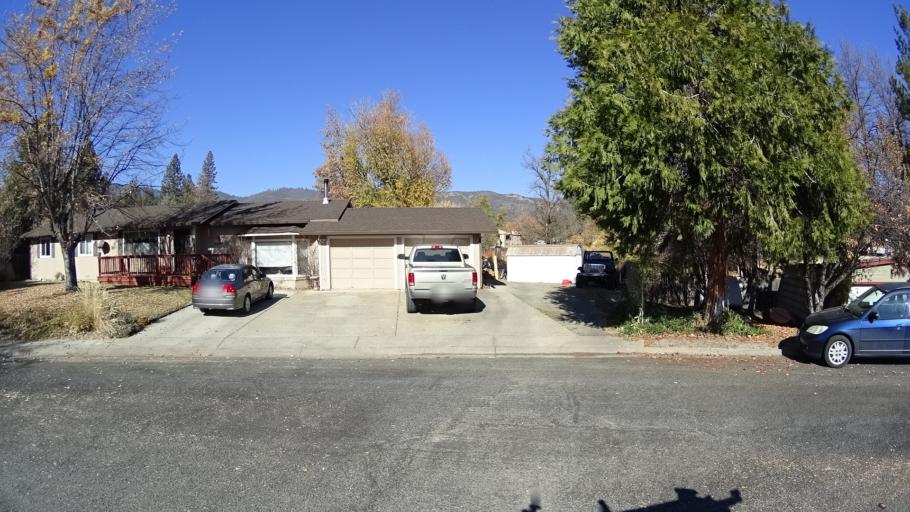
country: US
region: California
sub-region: Siskiyou County
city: Yreka
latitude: 41.7330
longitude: -122.6498
